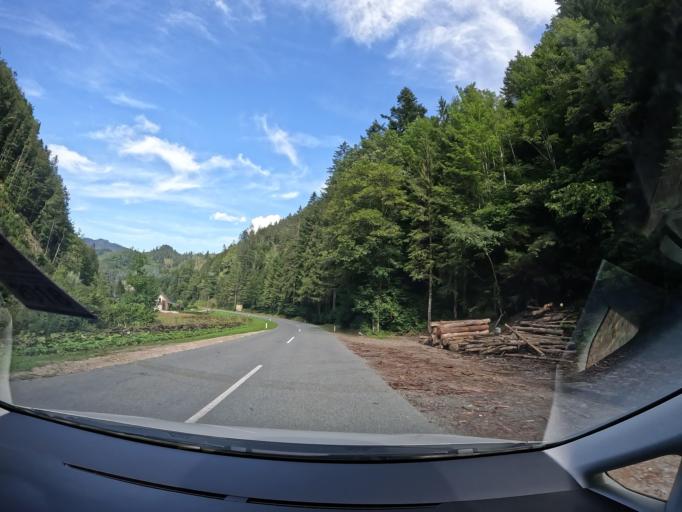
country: AT
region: Carinthia
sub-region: Politischer Bezirk Volkermarkt
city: Bad Eisenkappel
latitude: 46.4614
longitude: 14.5876
